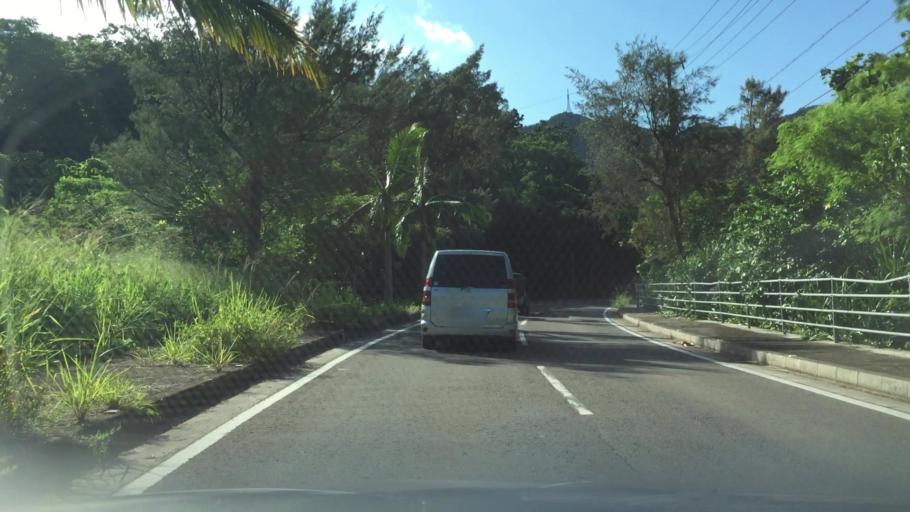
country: JP
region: Okinawa
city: Ishigaki
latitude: 24.4445
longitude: 124.1360
